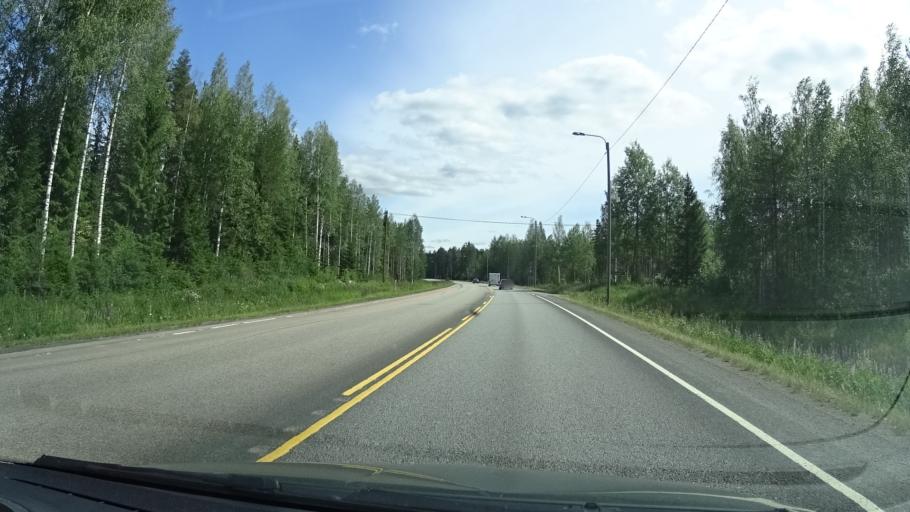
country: FI
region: Central Finland
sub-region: Jyvaeskylae
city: Muurame
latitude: 62.2672
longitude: 25.5208
